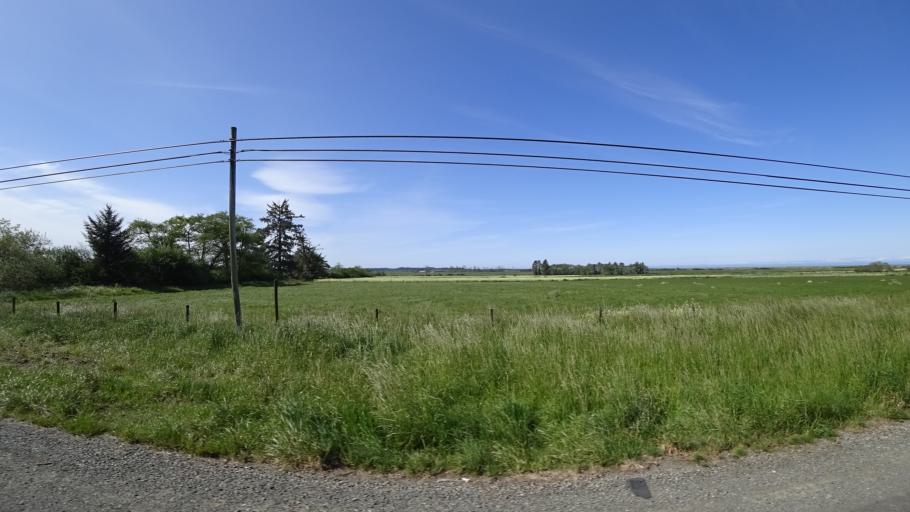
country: US
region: Oregon
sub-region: Curry County
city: Harbor
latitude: 41.9371
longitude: -124.1760
